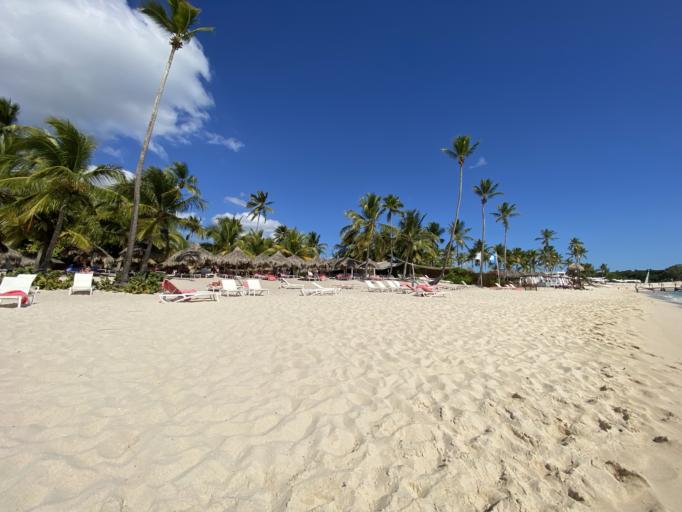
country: DO
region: La Romana
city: La Romana
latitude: 18.3425
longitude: -68.8226
